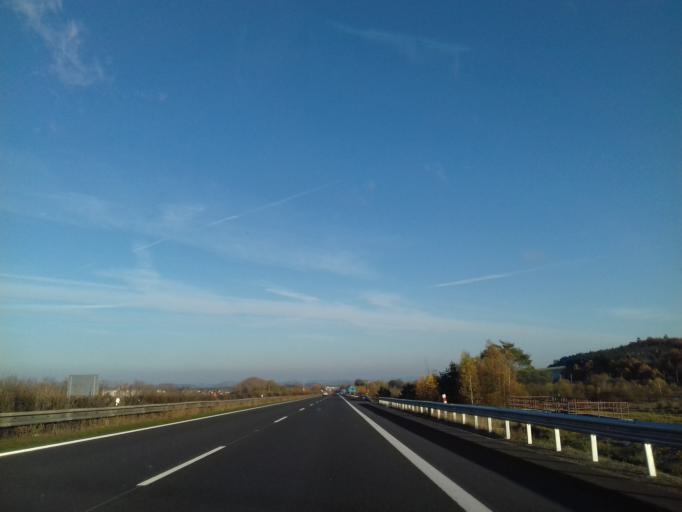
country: CZ
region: Plzensky
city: Zbiroh
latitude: 49.8391
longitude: 13.8072
